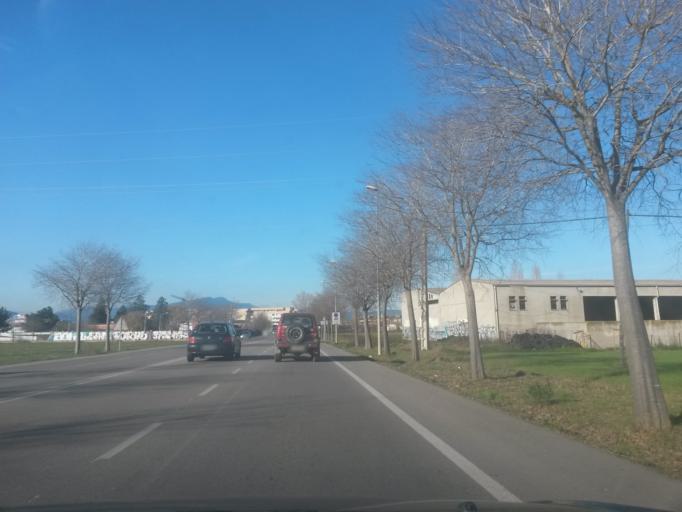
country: ES
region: Catalonia
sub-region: Provincia de Girona
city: Salt
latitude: 41.9639
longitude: 2.7897
